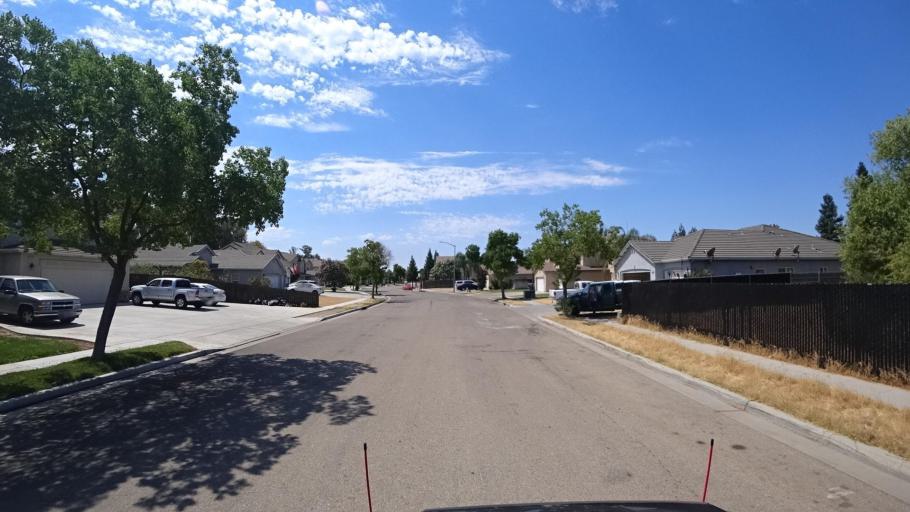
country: US
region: California
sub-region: Fresno County
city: Sunnyside
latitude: 36.7247
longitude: -119.7123
